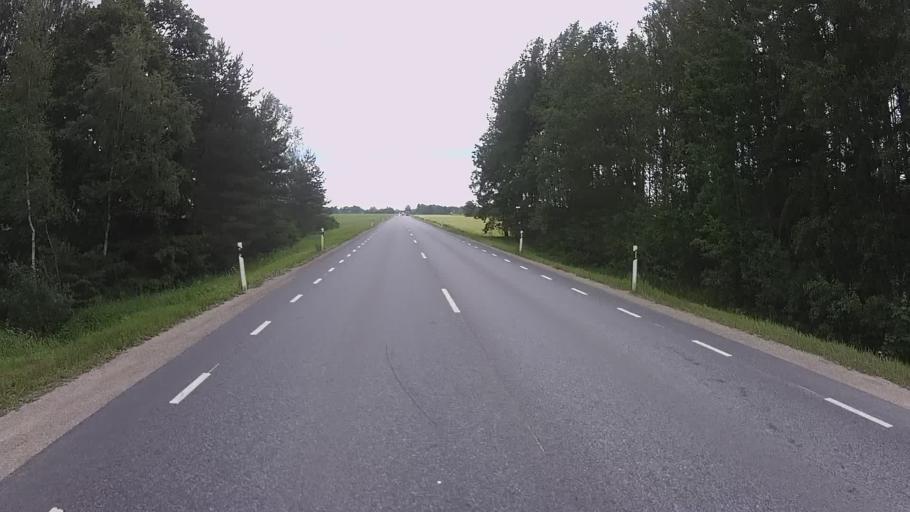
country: EE
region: Polvamaa
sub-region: Polva linn
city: Polva
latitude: 58.0811
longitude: 27.0361
